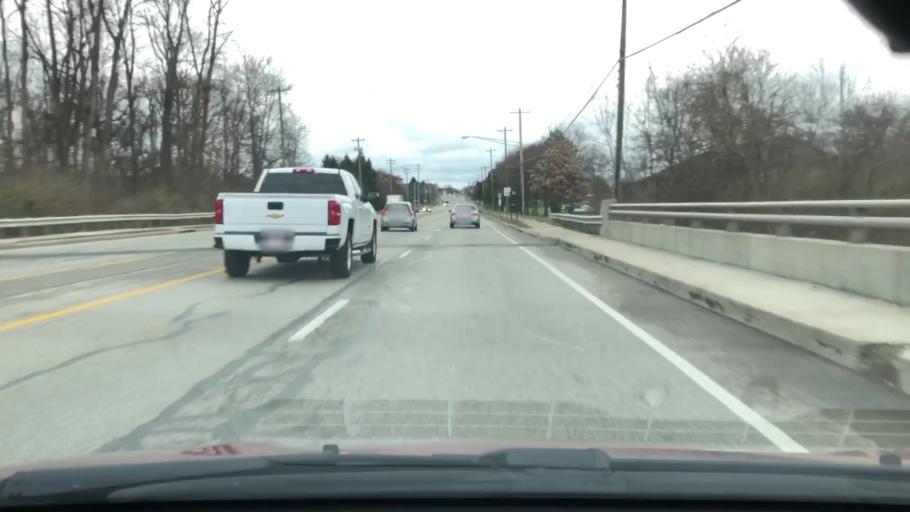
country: US
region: Ohio
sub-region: Franklin County
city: Westerville
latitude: 40.1103
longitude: -82.9395
